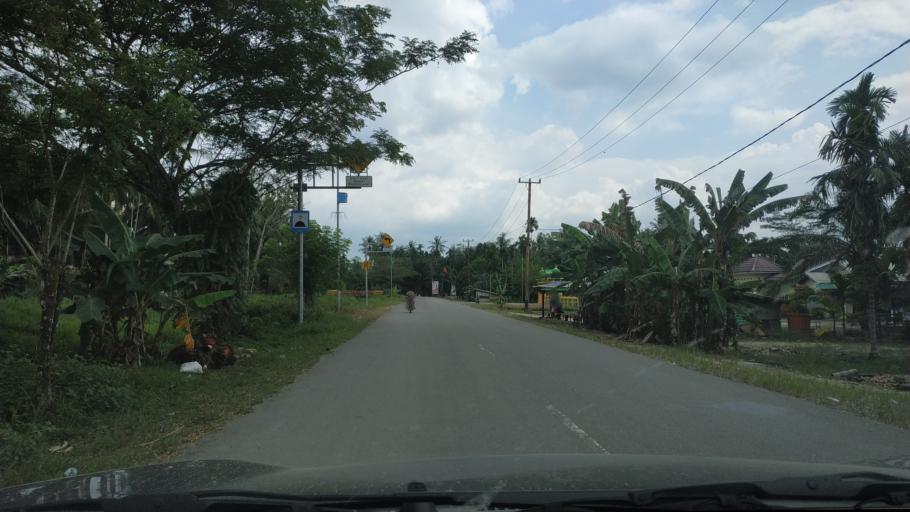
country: ID
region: Riau
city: Sungaisalak
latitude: -0.5667
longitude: 102.9681
